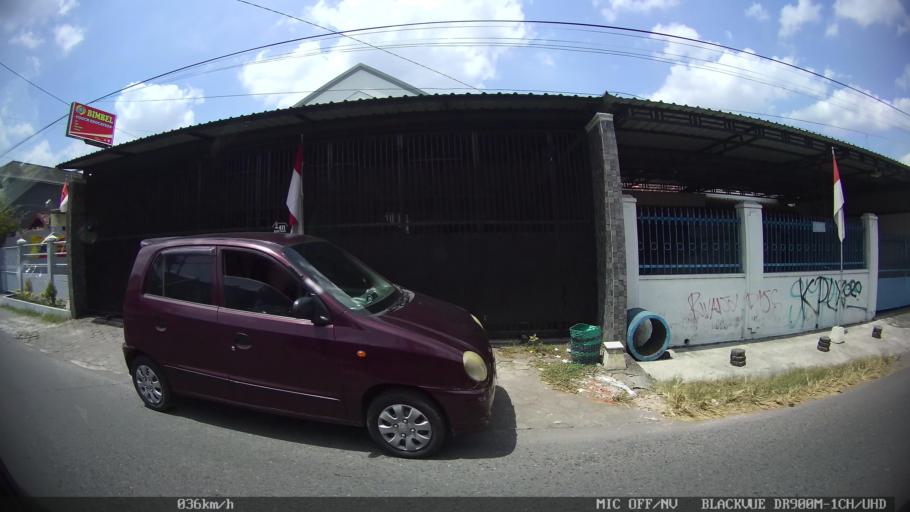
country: ID
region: Daerah Istimewa Yogyakarta
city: Gamping Lor
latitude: -7.8035
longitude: 110.3417
